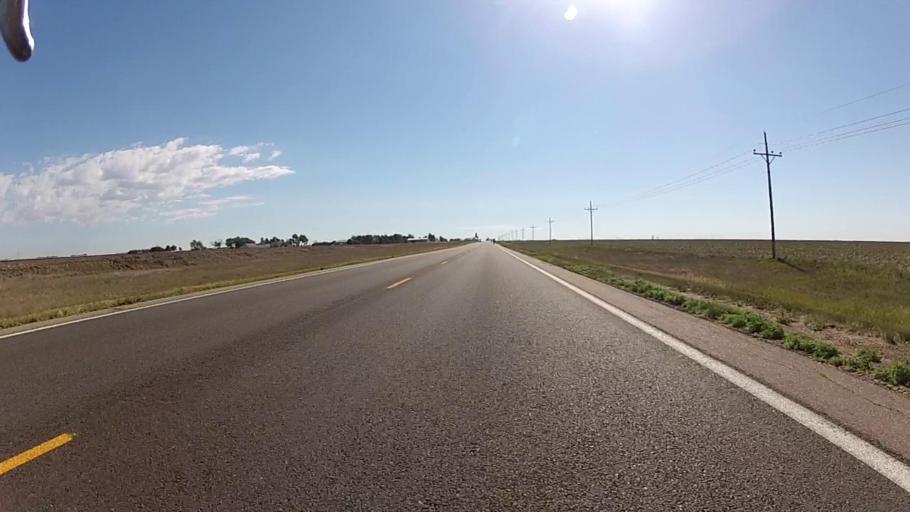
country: US
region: Kansas
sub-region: Gray County
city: Cimarron
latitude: 37.5880
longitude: -100.4830
